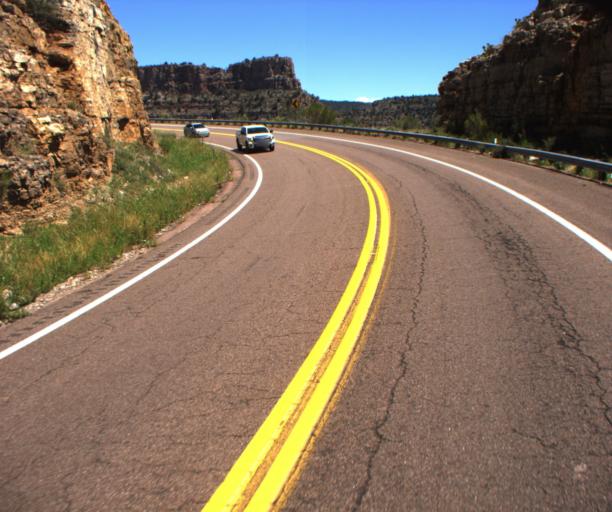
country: US
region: Arizona
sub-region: Navajo County
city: Cibecue
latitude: 33.8084
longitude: -110.4662
